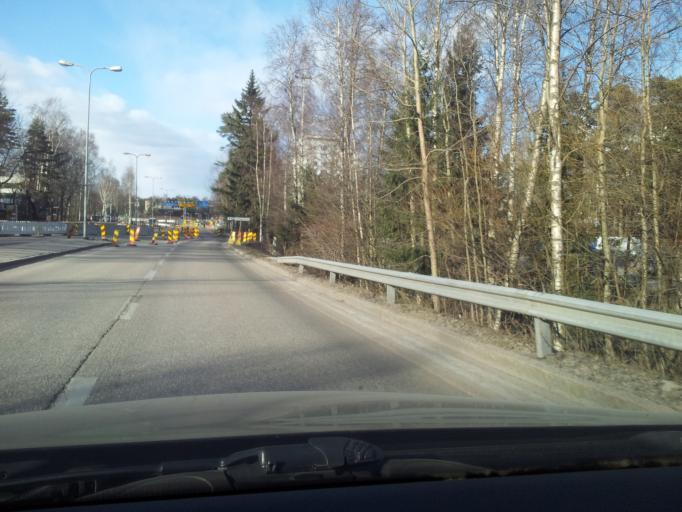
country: FI
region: Uusimaa
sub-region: Helsinki
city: Otaniemi
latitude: 60.1712
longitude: 24.8106
